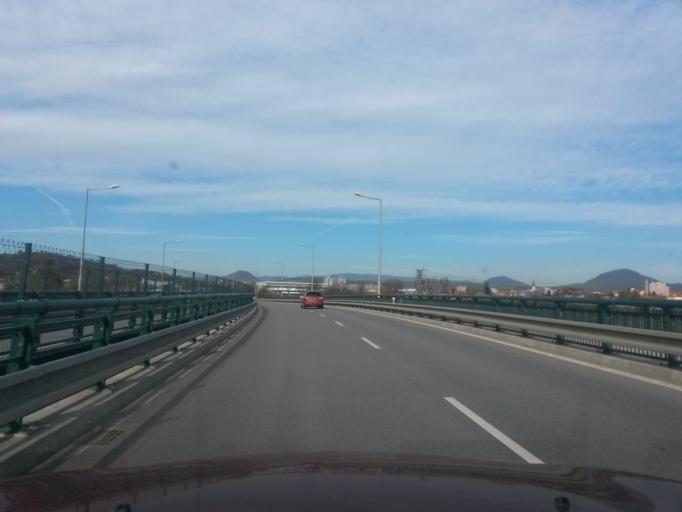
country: SK
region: Presovsky
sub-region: Okres Presov
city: Presov
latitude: 48.9795
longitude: 21.2400
